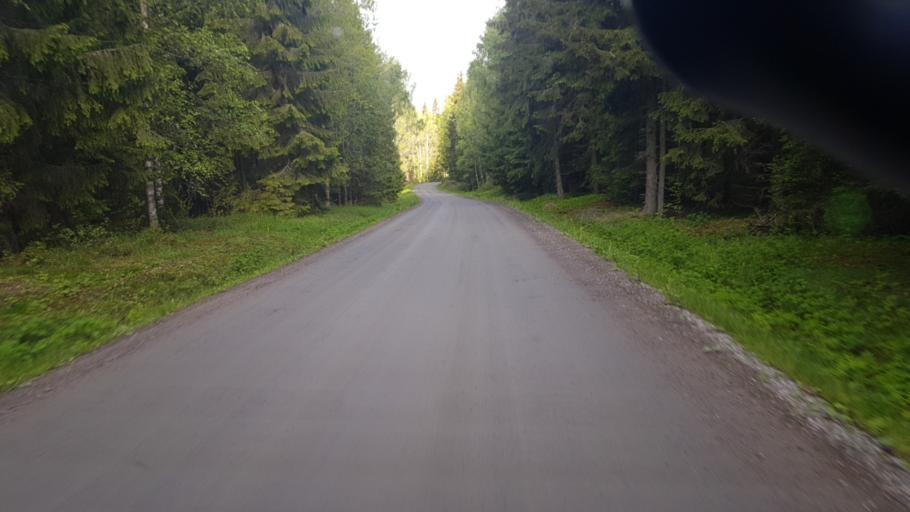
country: NO
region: Ostfold
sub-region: Romskog
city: Romskog
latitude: 59.8247
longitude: 11.9988
